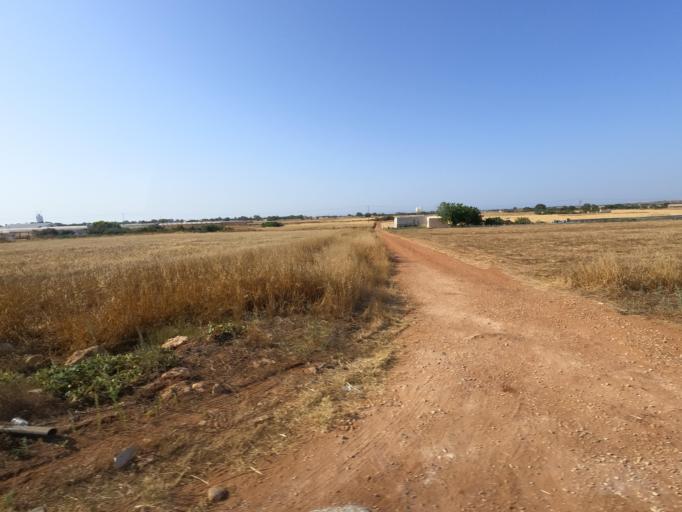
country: CY
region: Ammochostos
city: Liopetri
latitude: 34.9998
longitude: 33.9133
